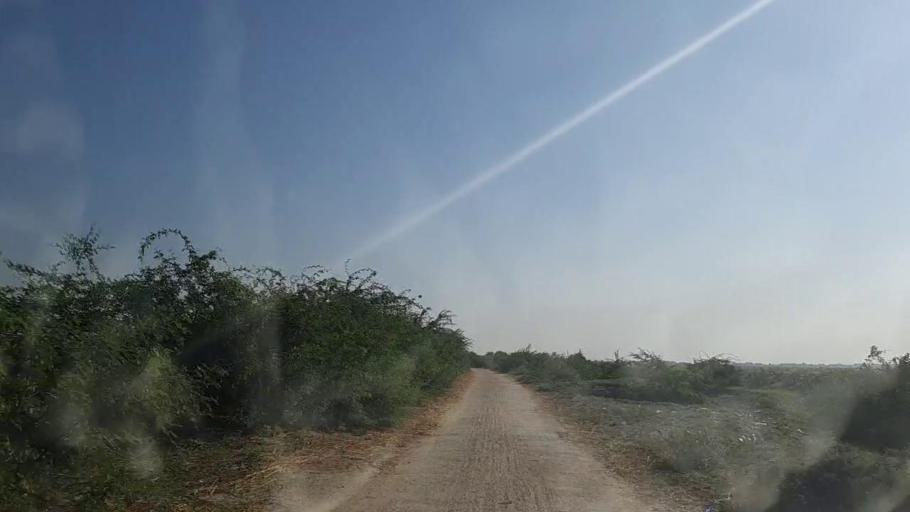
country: PK
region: Sindh
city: Mirpur Batoro
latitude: 24.6275
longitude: 68.1602
